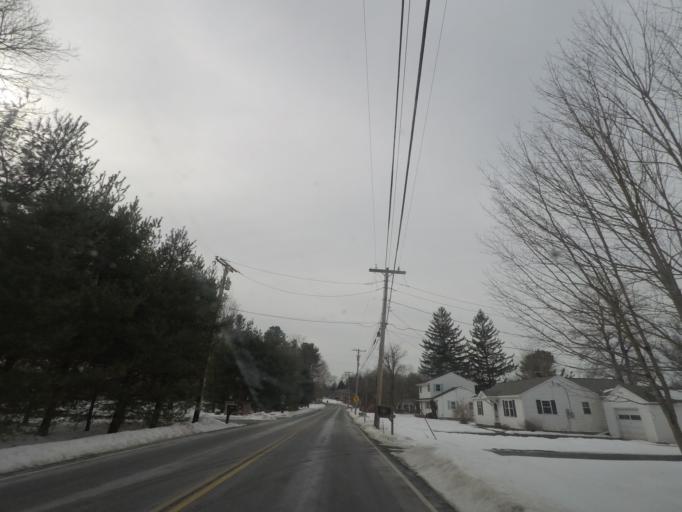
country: US
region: New York
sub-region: Albany County
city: Westmere
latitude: 42.6788
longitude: -73.8901
